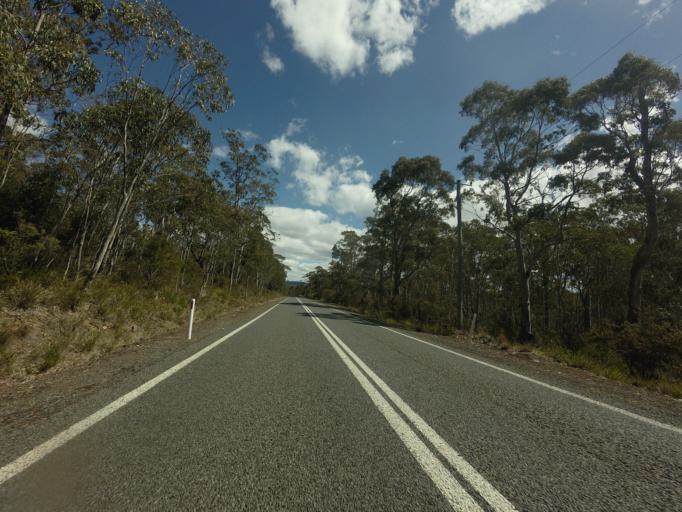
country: AU
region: Tasmania
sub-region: Northern Midlands
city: Evandale
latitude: -42.0270
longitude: 147.8355
